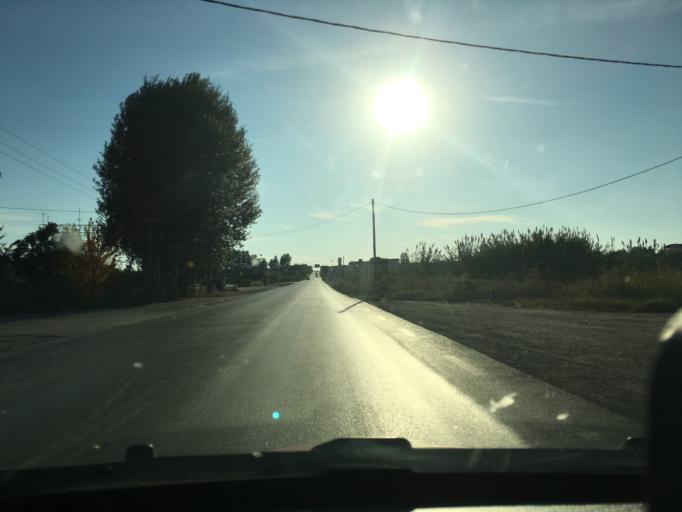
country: GR
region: Central Macedonia
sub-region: Nomos Chalkidikis
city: Nea Moudhania
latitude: 40.2506
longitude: 23.3142
